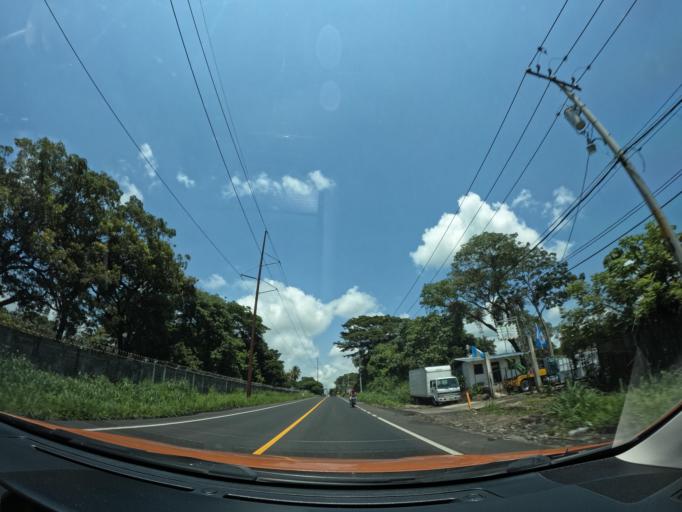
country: GT
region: Escuintla
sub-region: Municipio de Escuintla
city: Escuintla
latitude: 14.2661
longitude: -90.7948
